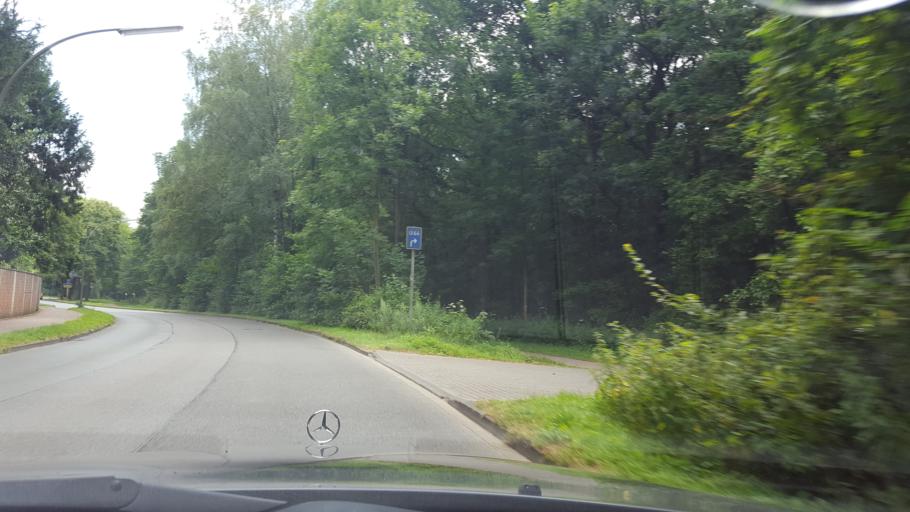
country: DE
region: North Rhine-Westphalia
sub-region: Regierungsbezirk Munster
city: Recklinghausen
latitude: 51.6595
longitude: 7.1799
